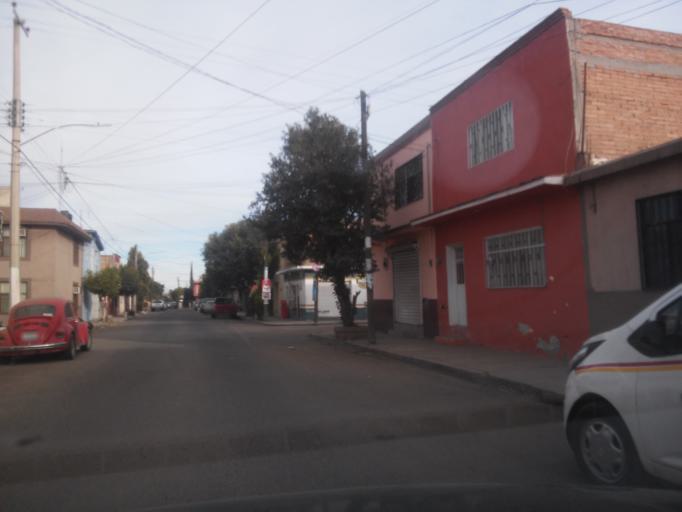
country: MX
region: Durango
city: Victoria de Durango
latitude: 24.0245
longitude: -104.6399
